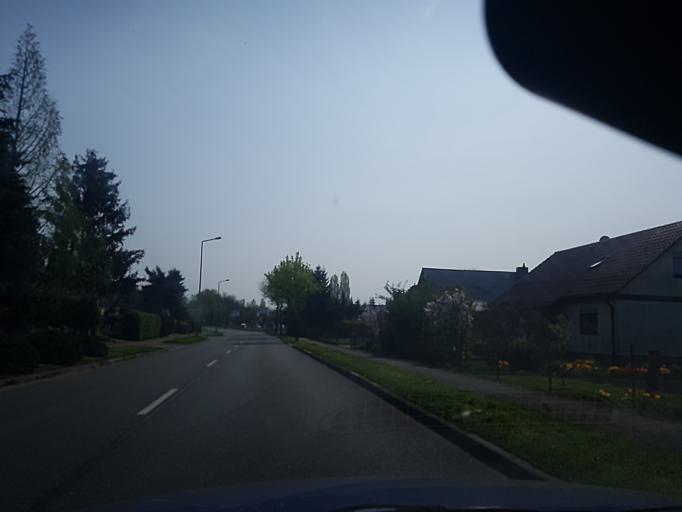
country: DE
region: Saxony
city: Beilrode
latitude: 51.5814
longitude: 13.0447
